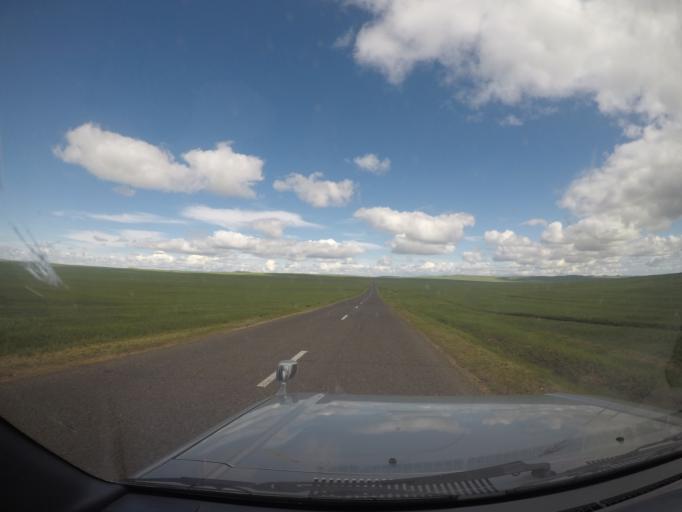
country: MN
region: Hentiy
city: Avraga
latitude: 47.4651
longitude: 109.6012
